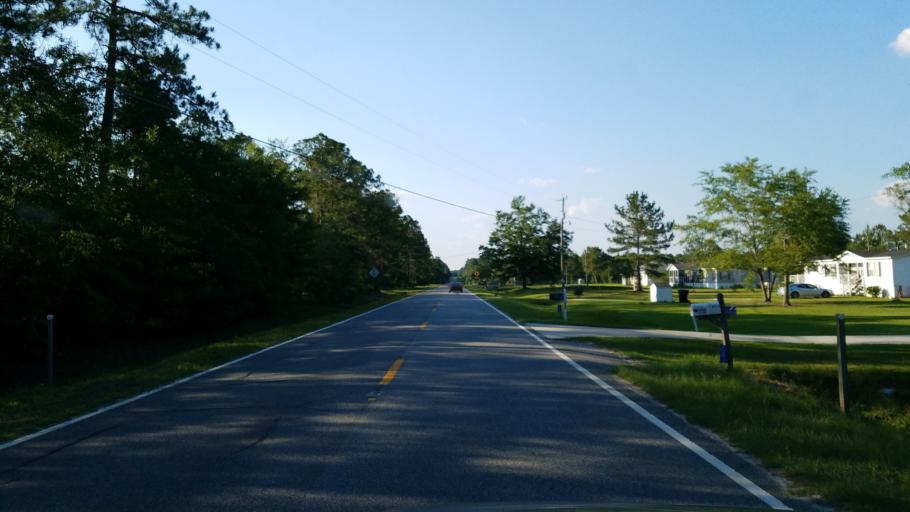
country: US
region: Georgia
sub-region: Lanier County
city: Lakeland
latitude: 30.9530
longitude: -83.0819
